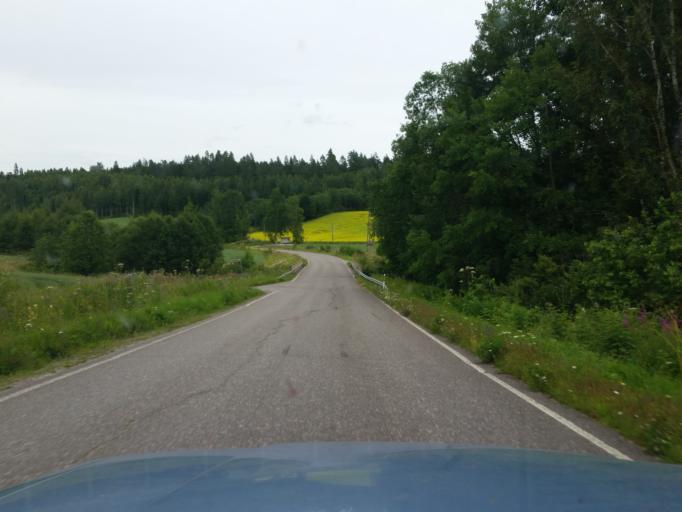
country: FI
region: Uusimaa
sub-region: Helsinki
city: Sammatti
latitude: 60.4367
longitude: 23.8387
